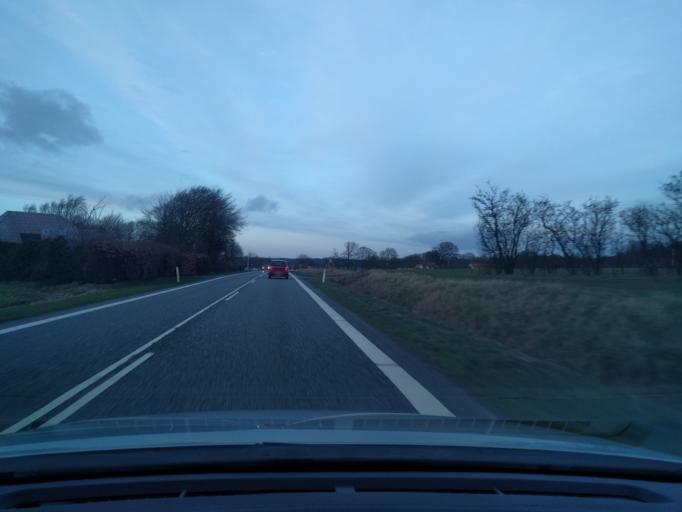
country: DK
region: South Denmark
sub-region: Tonder Kommune
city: Toftlund
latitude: 55.1522
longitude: 9.0292
